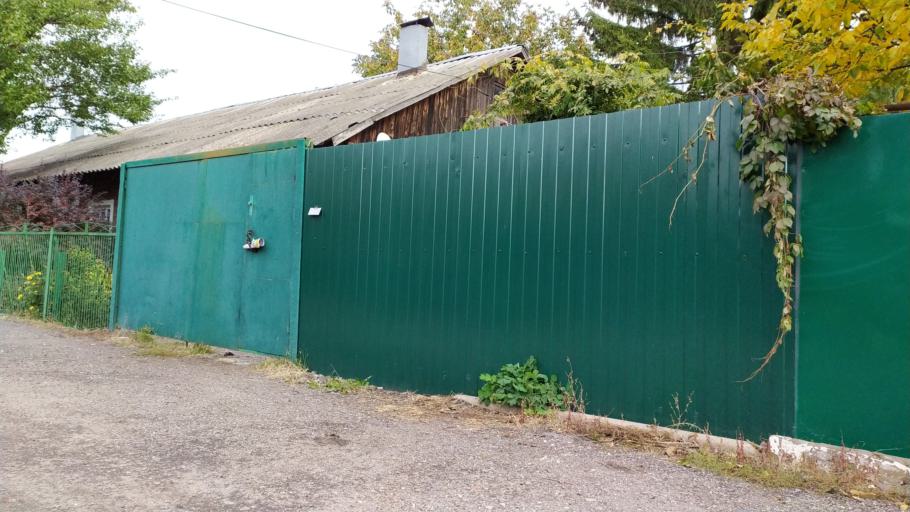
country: RU
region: Kursk
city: Kursk
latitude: 51.6494
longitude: 36.1484
